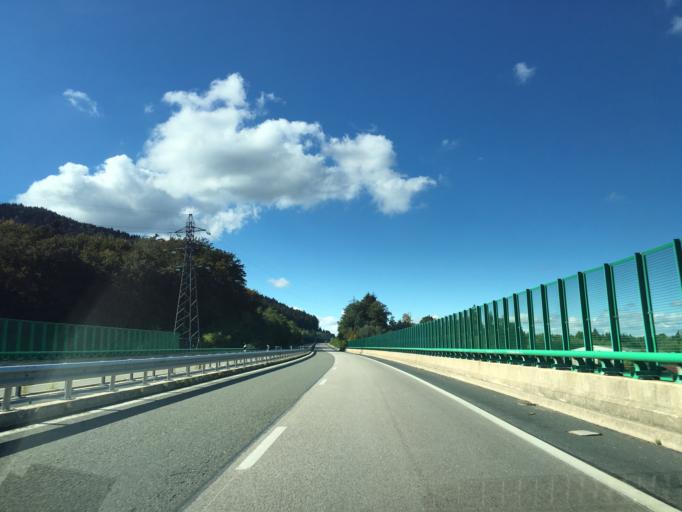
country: FR
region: Lorraine
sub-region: Departement des Vosges
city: Etival-Clairefontaine
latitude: 48.3930
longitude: 6.8578
